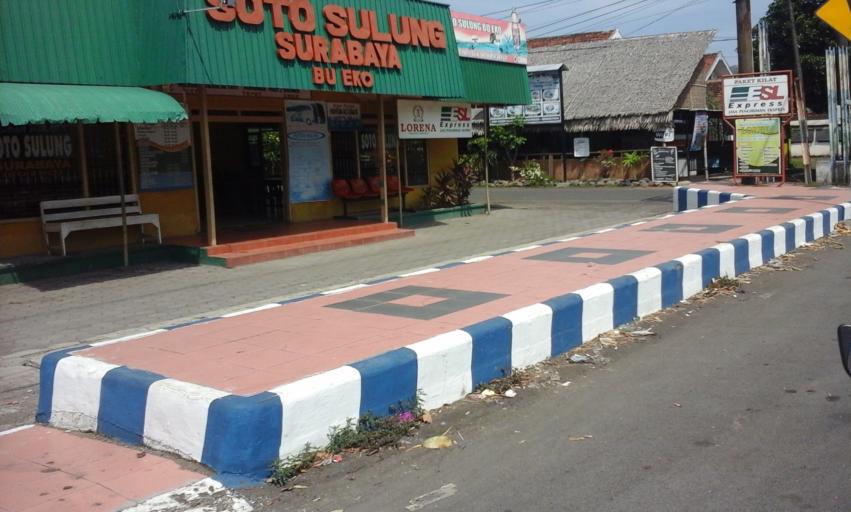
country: ID
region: East Java
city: Klatakan
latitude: -8.1410
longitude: 114.3990
